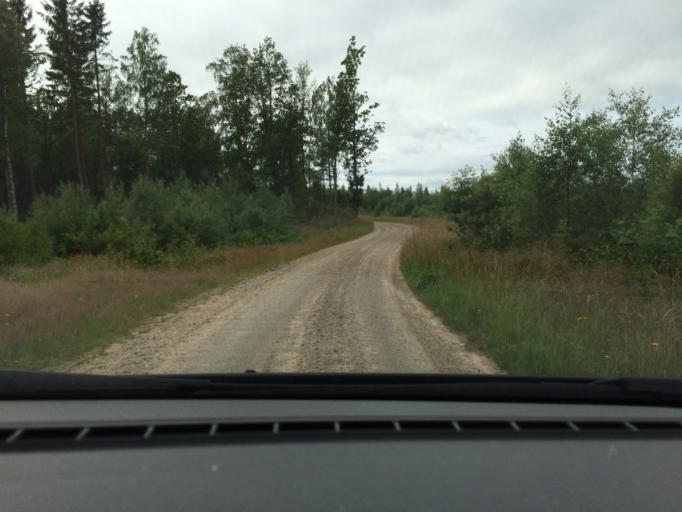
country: SE
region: Joenkoeping
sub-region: Varnamo Kommun
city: Forsheda
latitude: 57.0585
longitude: 13.7877
